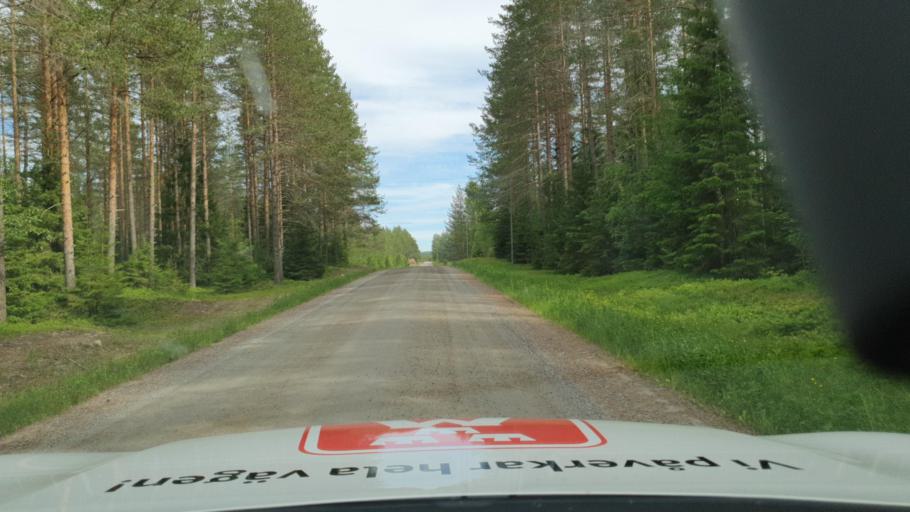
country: SE
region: Vaesterbotten
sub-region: Skelleftea Kommun
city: Burea
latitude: 64.3738
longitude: 21.0675
